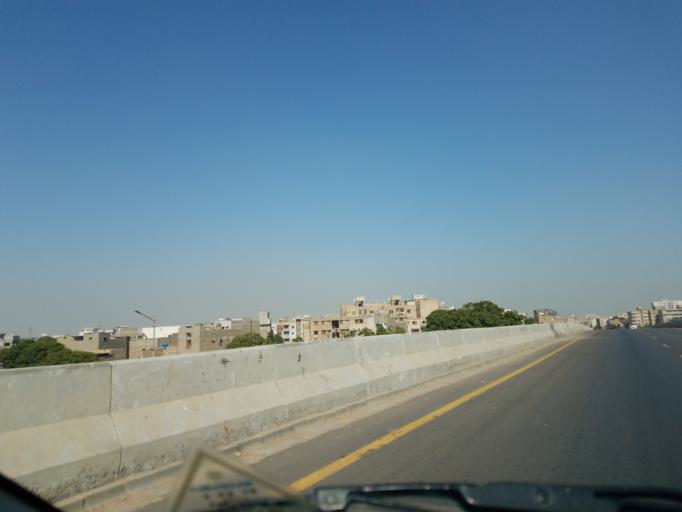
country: PK
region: Sindh
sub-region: Karachi District
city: Karachi
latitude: 24.8907
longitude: 67.0309
